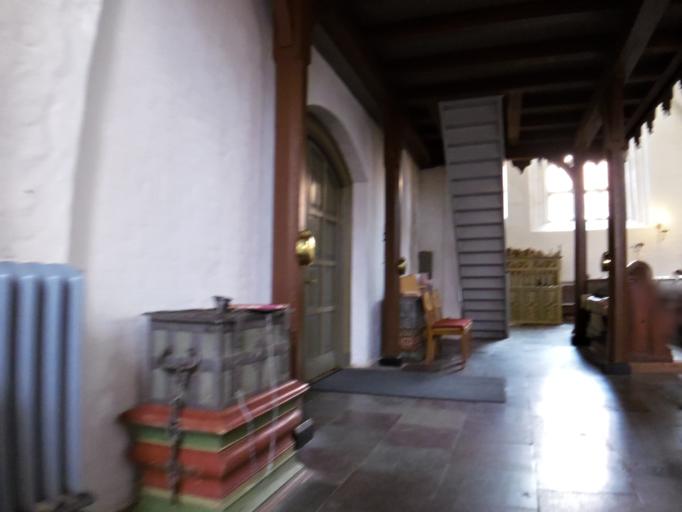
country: DK
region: South Denmark
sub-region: Tonder Kommune
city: Tonder
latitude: 54.9383
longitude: 8.8716
